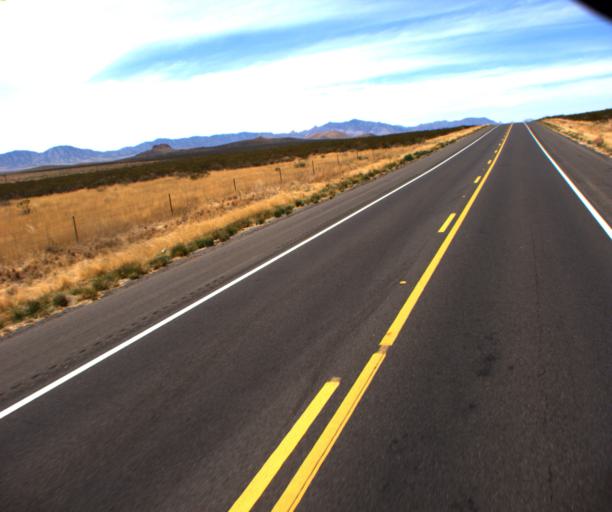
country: US
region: Arizona
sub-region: Cochise County
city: Willcox
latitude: 31.8994
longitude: -109.7061
